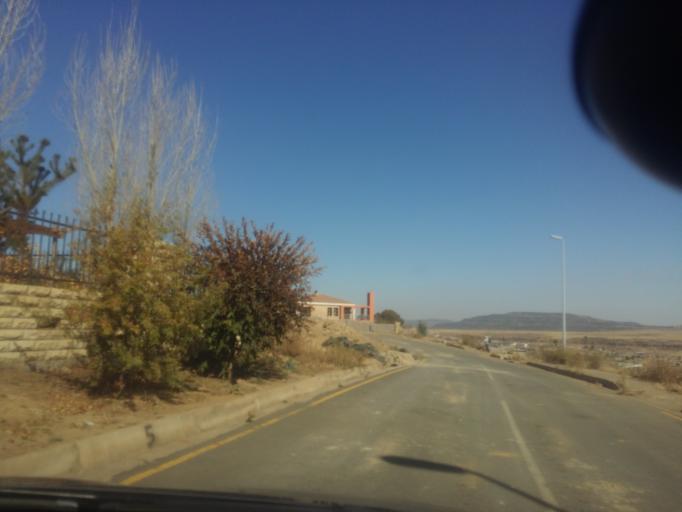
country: LS
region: Maseru
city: Maseru
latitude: -29.3431
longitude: 27.4452
